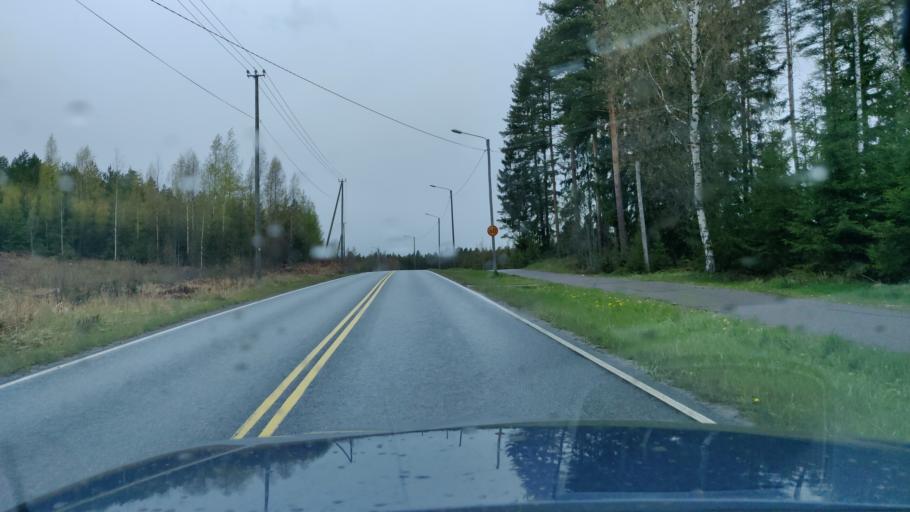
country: FI
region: Uusimaa
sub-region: Helsinki
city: Nurmijaervi
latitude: 60.5237
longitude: 24.7267
